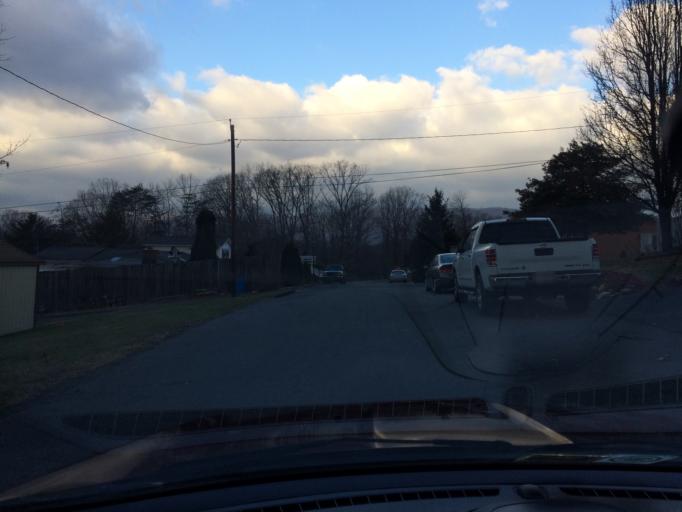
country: US
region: Virginia
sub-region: Alleghany County
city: Clifton Forge
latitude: 37.8284
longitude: -79.8184
